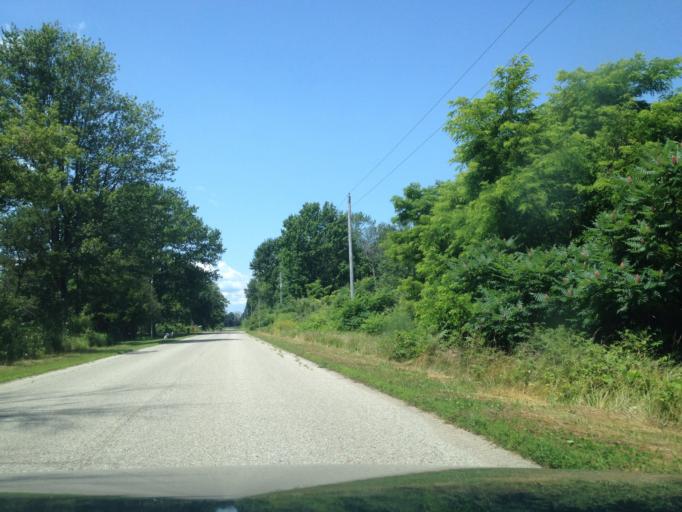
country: CA
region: Ontario
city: Aylmer
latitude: 42.6408
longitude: -80.7741
